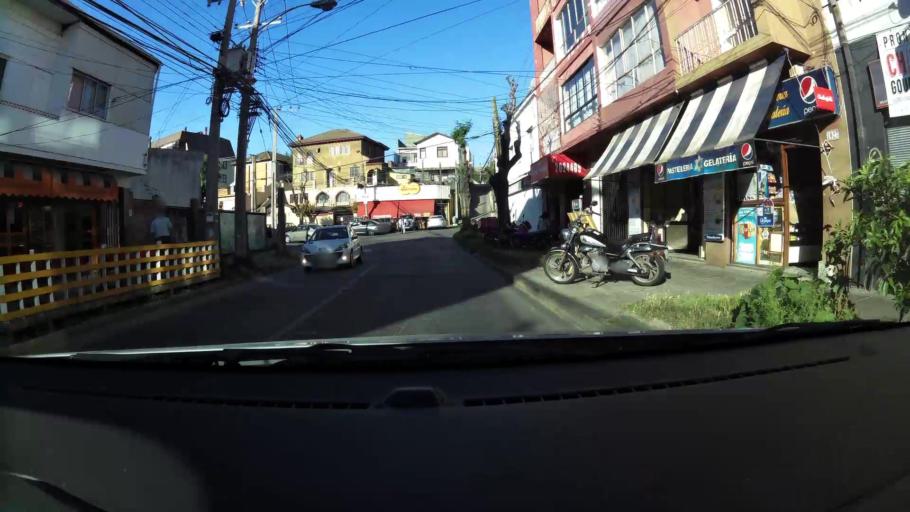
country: CL
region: Valparaiso
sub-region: Provincia de Valparaiso
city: Vina del Mar
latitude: -33.0277
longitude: -71.5739
